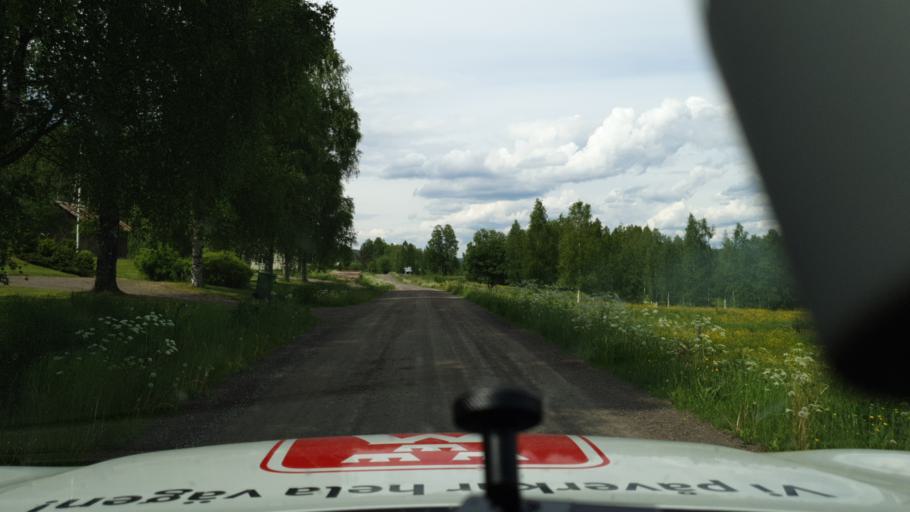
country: SE
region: Vaermland
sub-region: Torsby Kommun
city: Torsby
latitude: 59.9711
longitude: 12.8648
